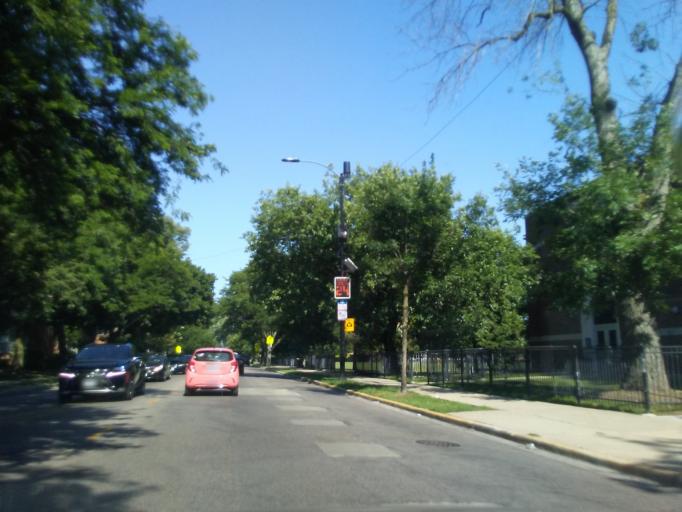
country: US
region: Illinois
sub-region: Cook County
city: Lincolnwood
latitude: 41.9760
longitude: -87.6832
